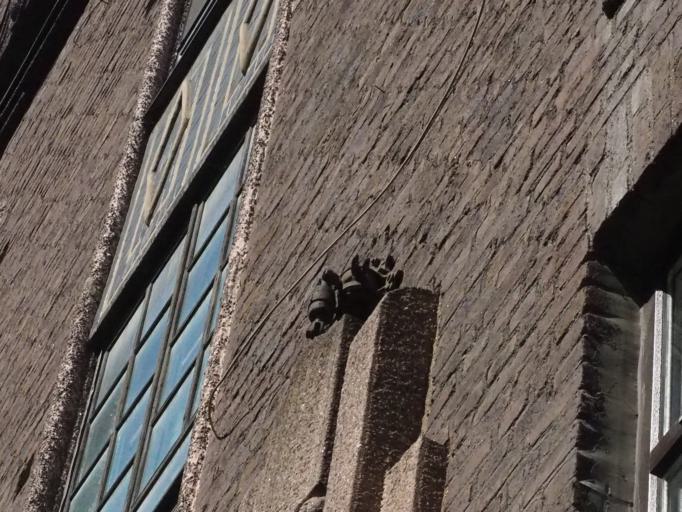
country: RU
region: Leningrad
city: Vyborg
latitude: 60.7076
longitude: 28.7472
